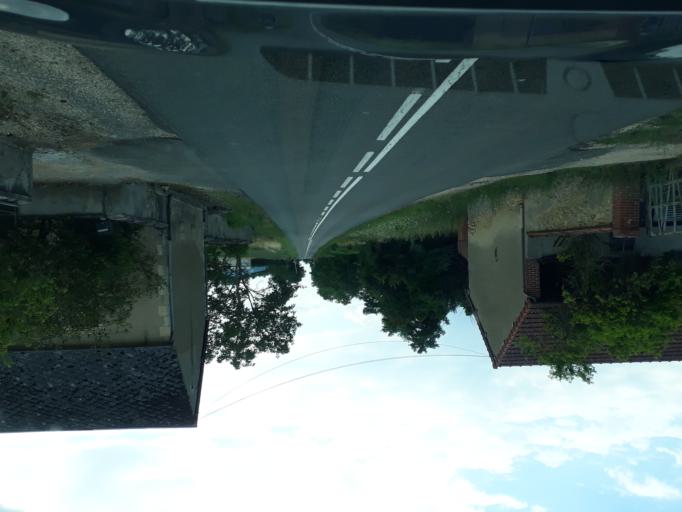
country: FR
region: Centre
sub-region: Departement du Cher
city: Jouet-sur-l'Aubois
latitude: 46.9658
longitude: 2.9631
